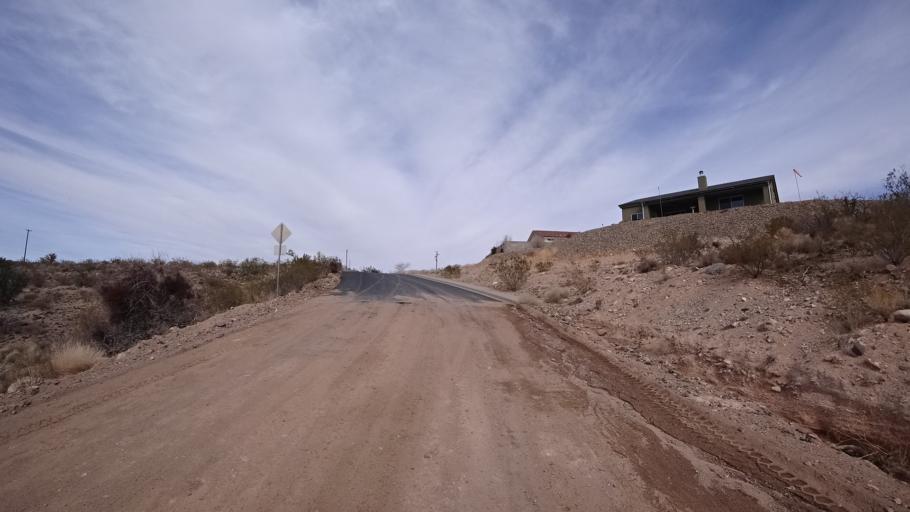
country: US
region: Arizona
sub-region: Mohave County
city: Kingman
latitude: 35.1848
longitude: -114.0187
